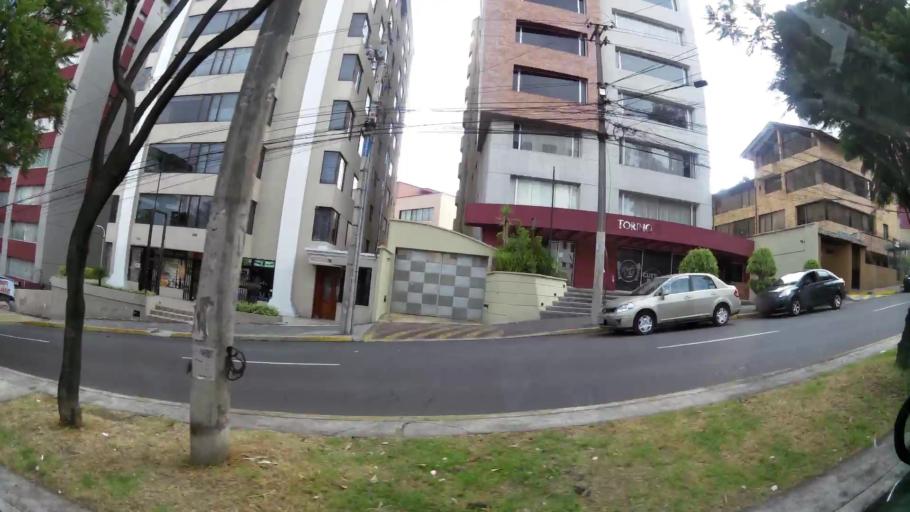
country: EC
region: Pichincha
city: Quito
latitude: -0.1715
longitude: -78.4728
